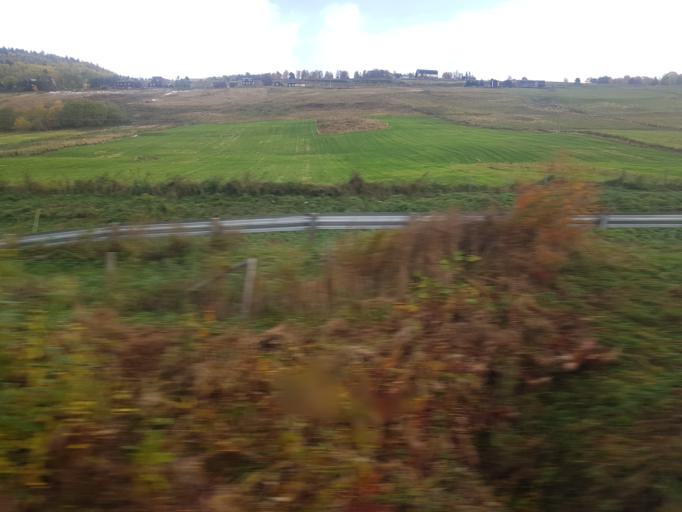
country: NO
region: Oppland
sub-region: Dovre
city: Dovre
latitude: 61.9708
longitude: 9.2556
